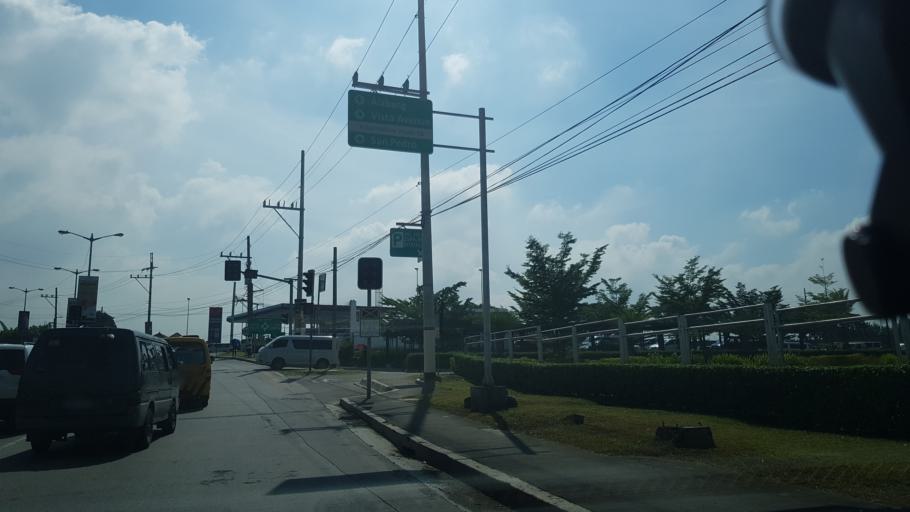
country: PH
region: Calabarzon
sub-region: Province of Laguna
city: San Pedro
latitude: 14.3746
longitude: 121.0109
